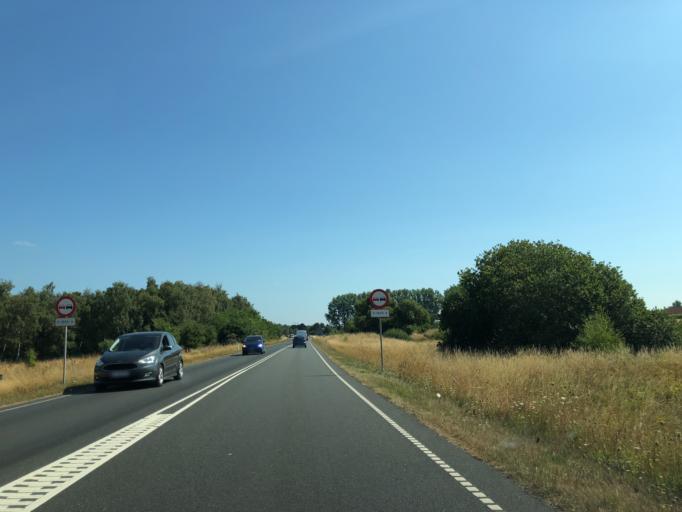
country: DK
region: Zealand
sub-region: Odsherred Kommune
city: Nykobing Sjaelland
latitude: 55.9313
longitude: 11.6616
